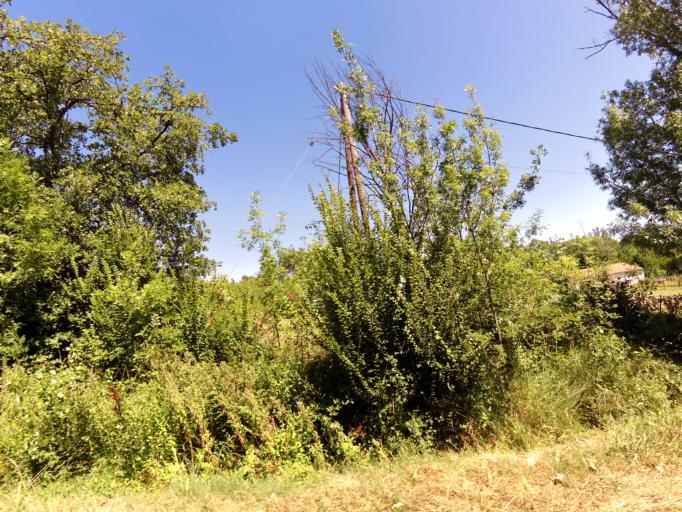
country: FR
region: Languedoc-Roussillon
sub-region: Departement du Gard
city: Boisset-et-Gaujac
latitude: 44.0269
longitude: 3.9955
